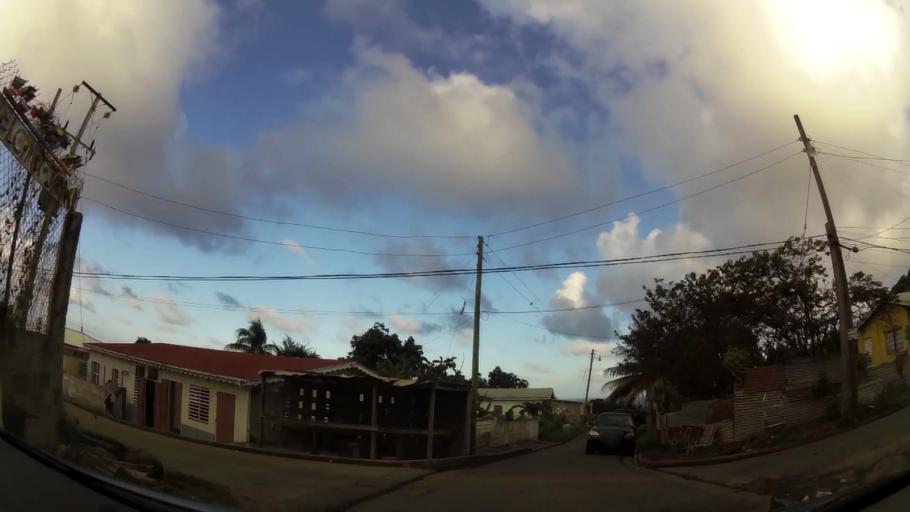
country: KN
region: Saint Mary Cayon
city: Cayon
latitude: 17.3522
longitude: -62.7320
